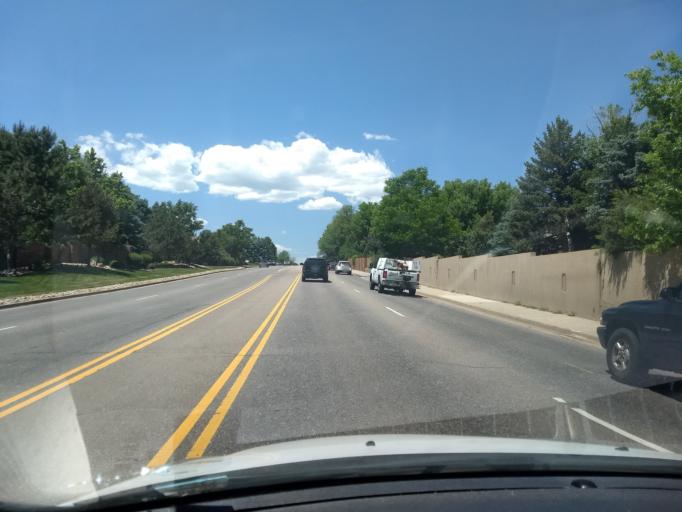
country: US
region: Colorado
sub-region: Arapahoe County
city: Greenwood Village
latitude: 39.6242
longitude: -104.9672
